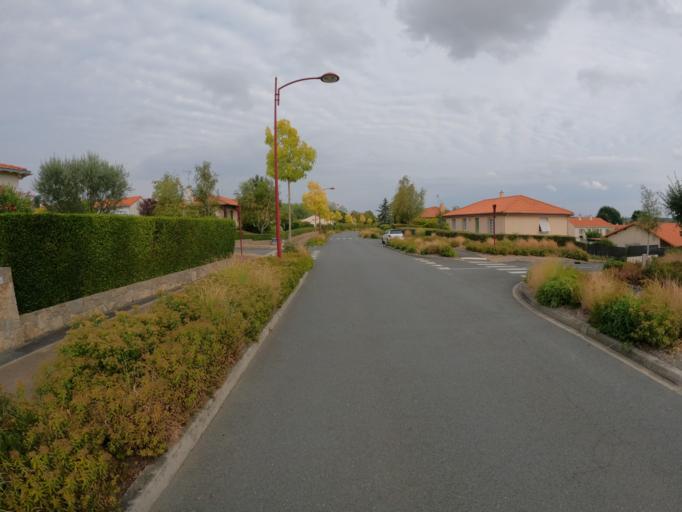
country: FR
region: Pays de la Loire
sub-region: Departement de Maine-et-Loire
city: La Seguiniere
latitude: 47.0624
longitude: -0.9363
